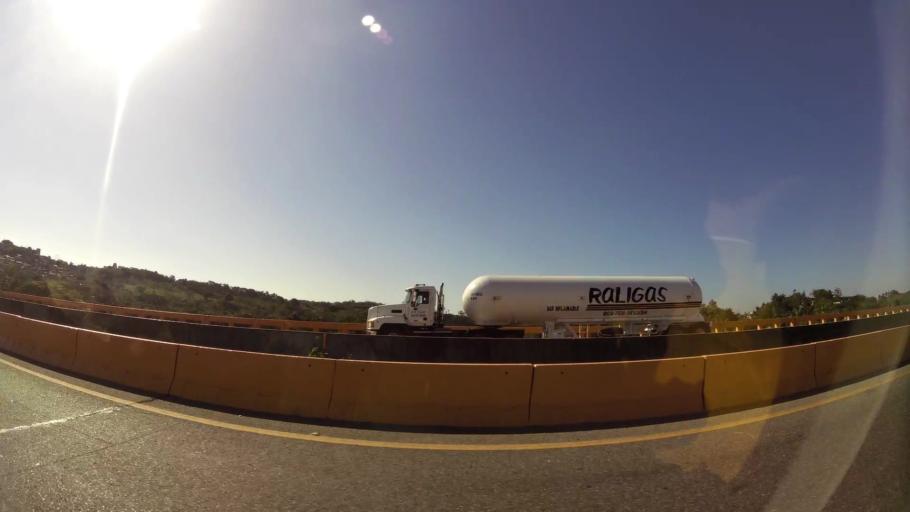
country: DO
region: San Cristobal
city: El Carril
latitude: 18.4395
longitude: -70.0075
